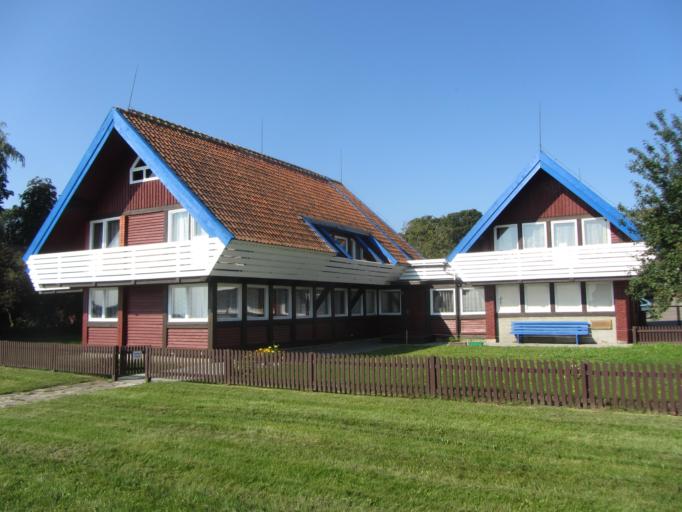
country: LT
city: Nida
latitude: 55.3080
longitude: 21.0087
